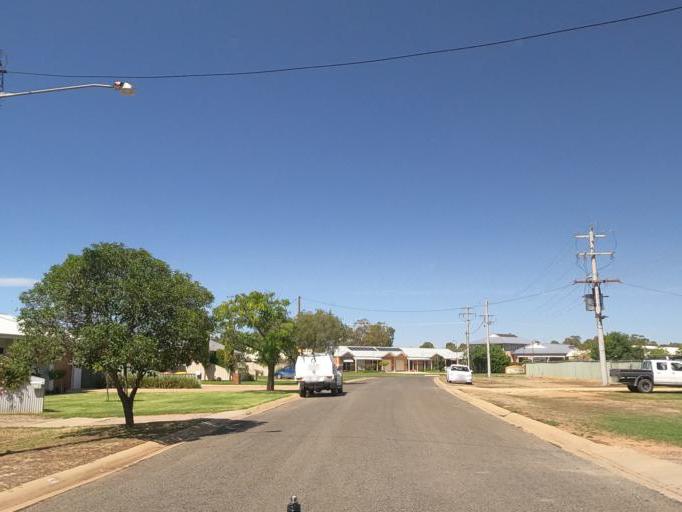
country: AU
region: New South Wales
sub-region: Corowa Shire
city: Mulwala
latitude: -35.9850
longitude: 146.0039
